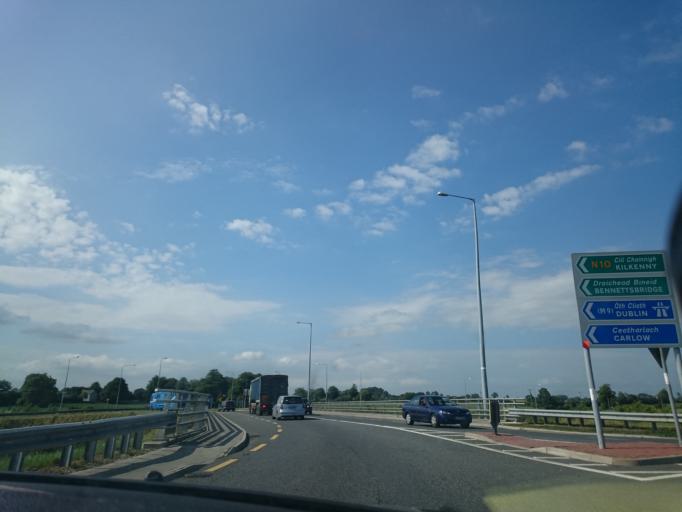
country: IE
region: Leinster
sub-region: Kilkenny
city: Kilkenny
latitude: 52.5724
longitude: -7.2320
